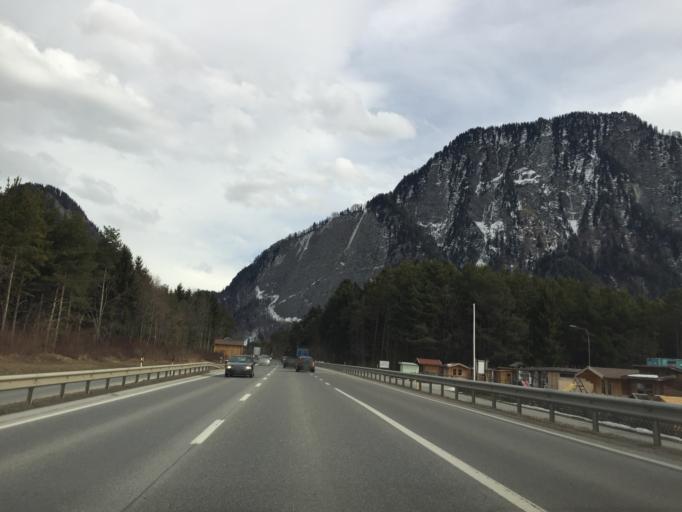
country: CH
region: Grisons
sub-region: Landquart District
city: Malans
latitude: 46.9690
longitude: 9.5795
